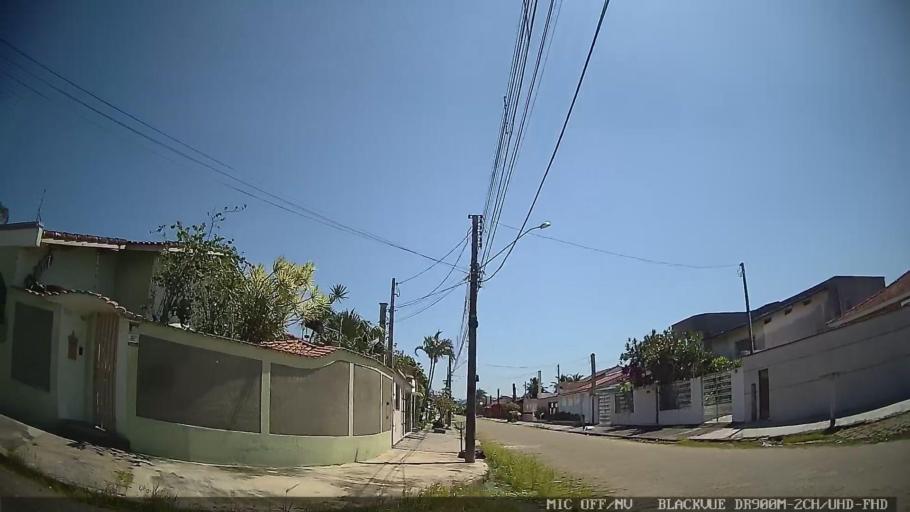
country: BR
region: Sao Paulo
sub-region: Peruibe
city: Peruibe
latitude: -24.2921
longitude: -46.9696
